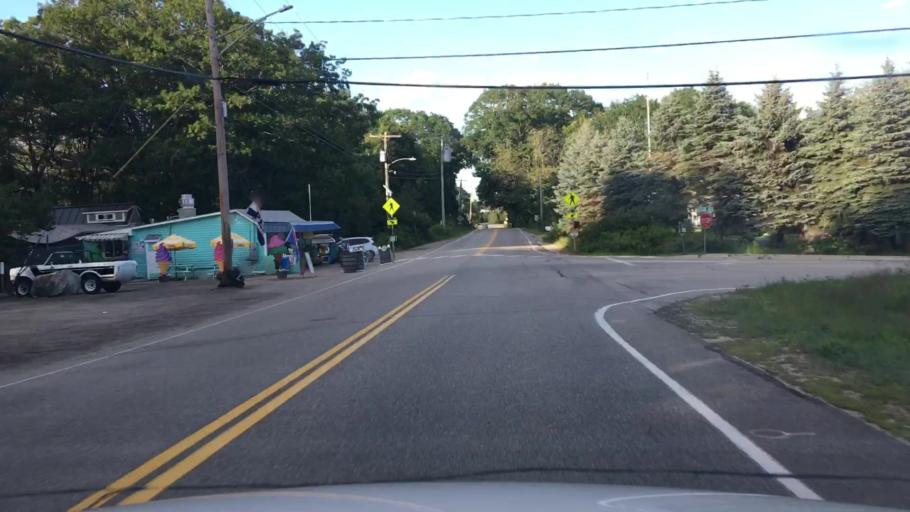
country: US
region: Maine
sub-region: Cumberland County
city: Scarborough
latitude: 43.5663
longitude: -70.2851
